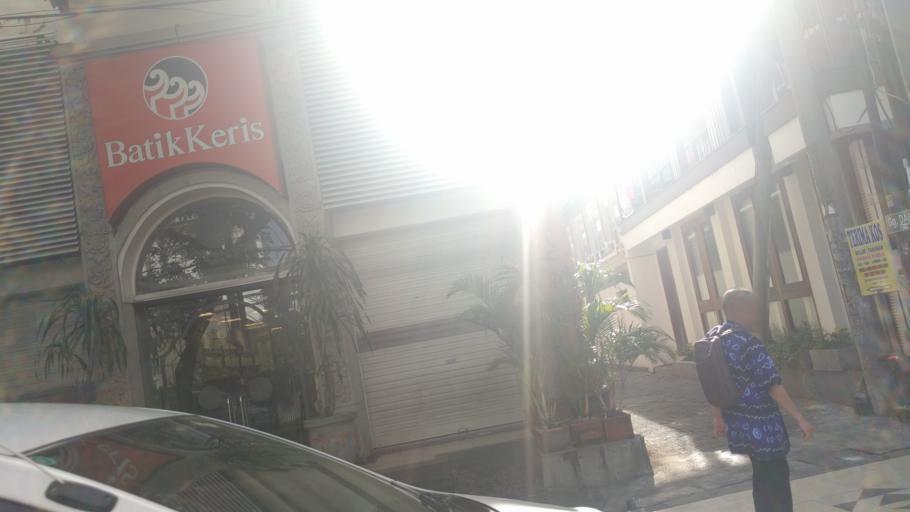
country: ID
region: Bali
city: Kuta
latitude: -8.7130
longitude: 115.1732
